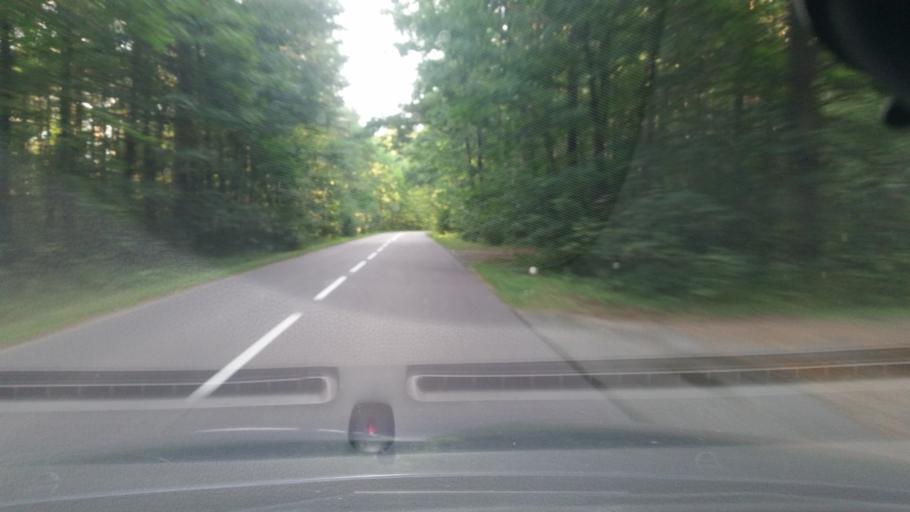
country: PL
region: Pomeranian Voivodeship
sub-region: Powiat wejherowski
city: Choczewo
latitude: 54.7544
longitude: 17.7476
